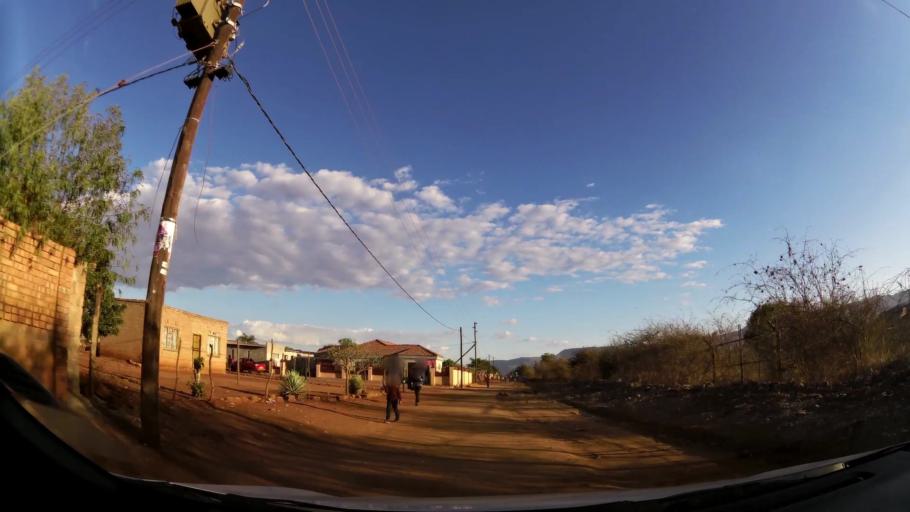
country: ZA
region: Limpopo
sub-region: Waterberg District Municipality
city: Mokopane
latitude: -24.1494
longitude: 28.9949
